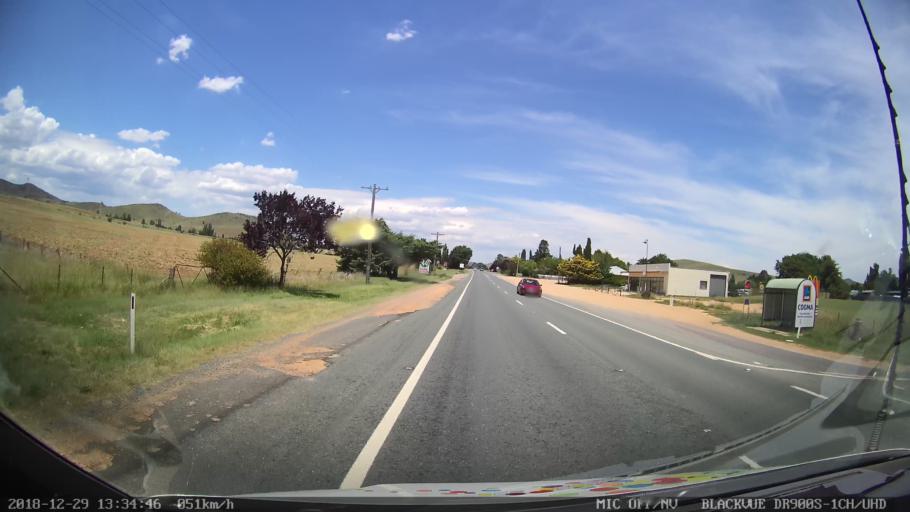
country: AU
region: New South Wales
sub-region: Cooma-Monaro
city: Cooma
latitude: -35.9550
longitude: 149.1480
